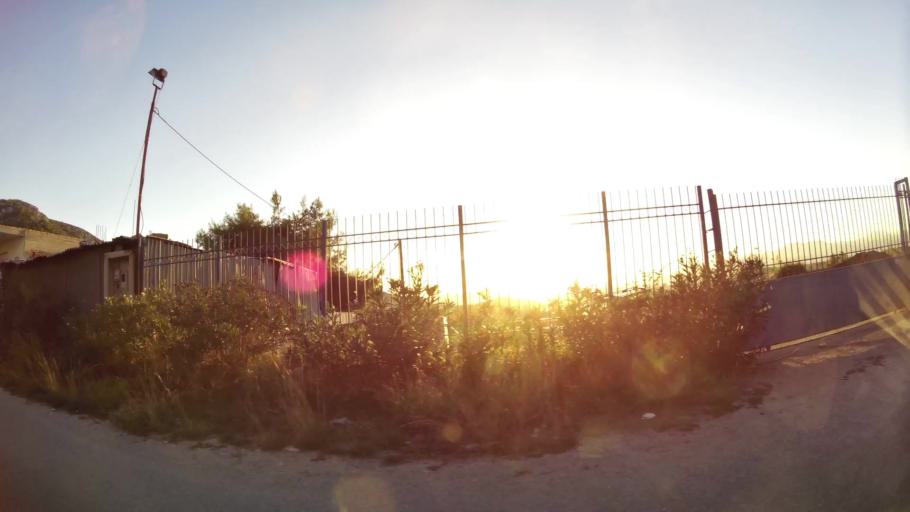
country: GR
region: Attica
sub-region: Nomarchia Athinas
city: Chaidari
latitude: 38.0380
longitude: 23.6374
